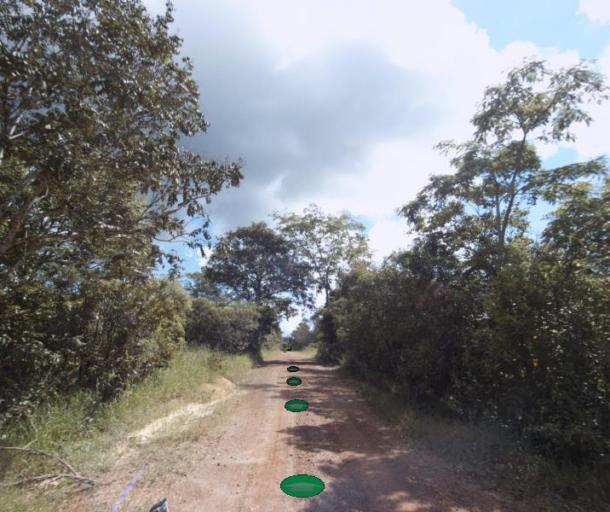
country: BR
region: Goias
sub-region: Pirenopolis
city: Pirenopolis
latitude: -15.7883
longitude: -48.8728
